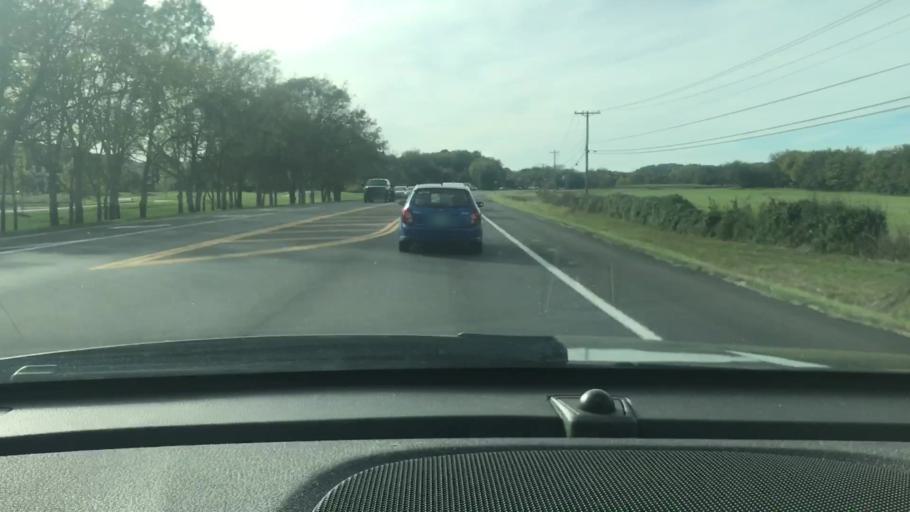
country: US
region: Tennessee
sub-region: Williamson County
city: Franklin
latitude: 35.9307
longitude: -86.9195
